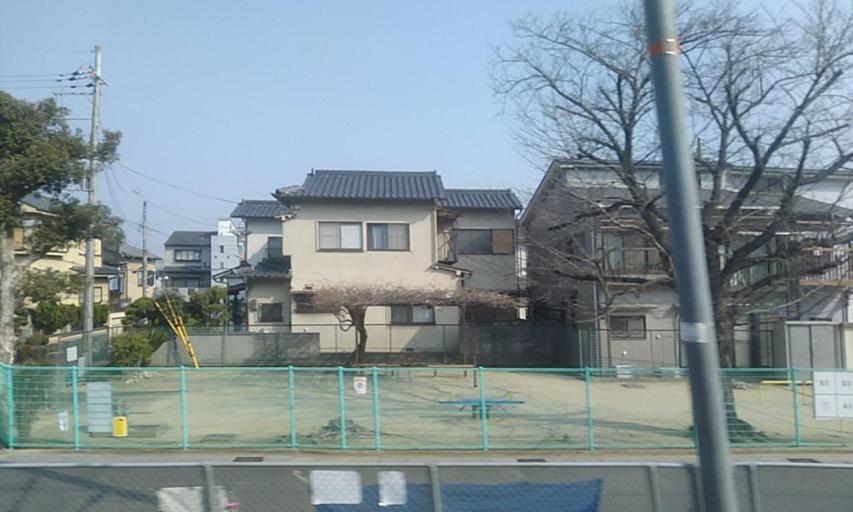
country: JP
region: Kyoto
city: Uji
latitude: 34.8890
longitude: 135.7899
